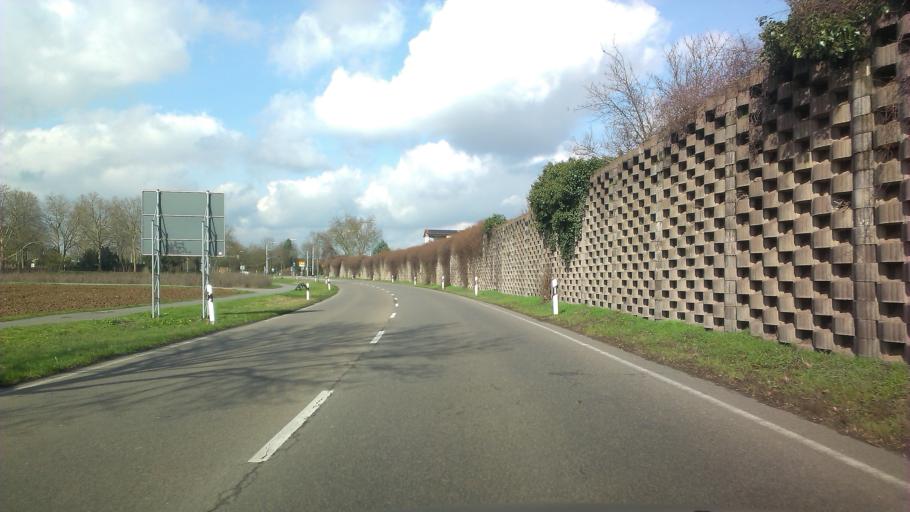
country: DE
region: Baden-Wuerttemberg
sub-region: Karlsruhe Region
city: Sandhausen
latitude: 49.3740
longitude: 8.6618
